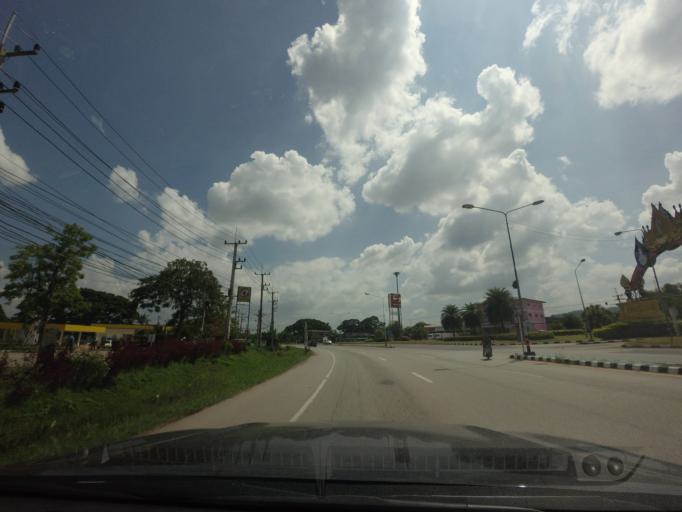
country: TH
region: Phetchabun
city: Phetchabun
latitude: 16.2622
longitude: 101.0480
